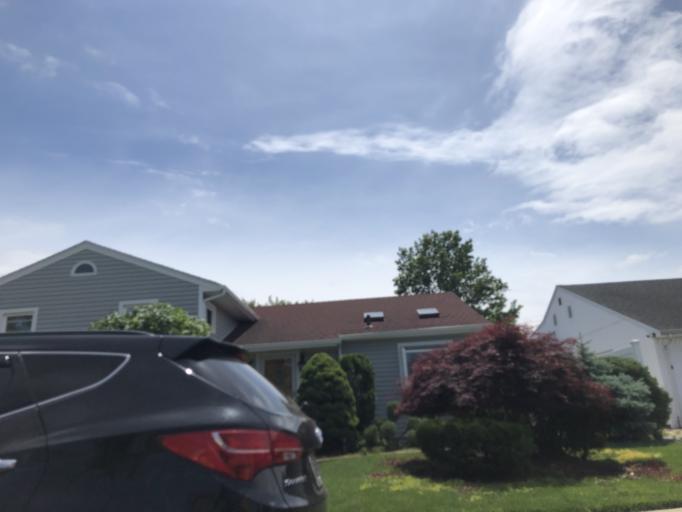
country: US
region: New York
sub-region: Nassau County
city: South Valley Stream
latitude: 40.6586
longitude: -73.7220
